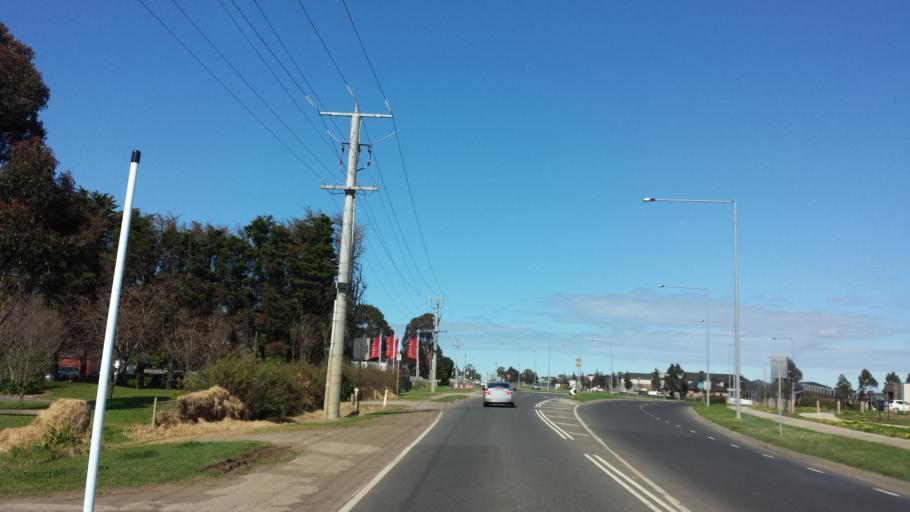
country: AU
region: Victoria
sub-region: Casey
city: Cranbourne East
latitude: -38.1094
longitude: 145.3291
